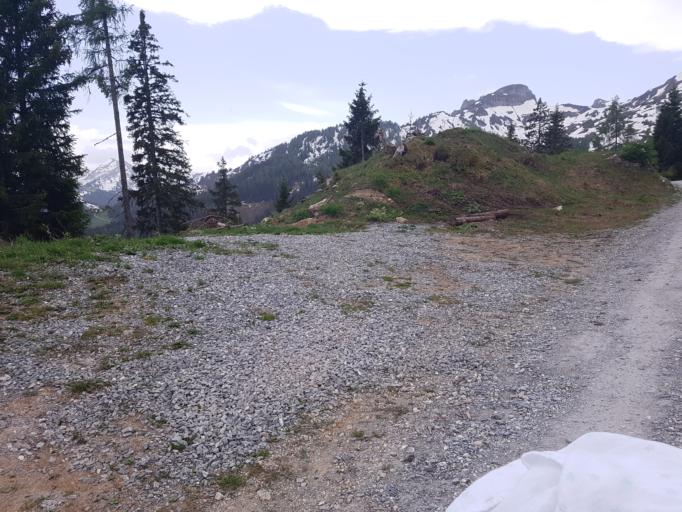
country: AT
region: Salzburg
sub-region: Politischer Bezirk Sankt Johann im Pongau
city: Schwarzach im Pongau
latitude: 47.2793
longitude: 13.1863
